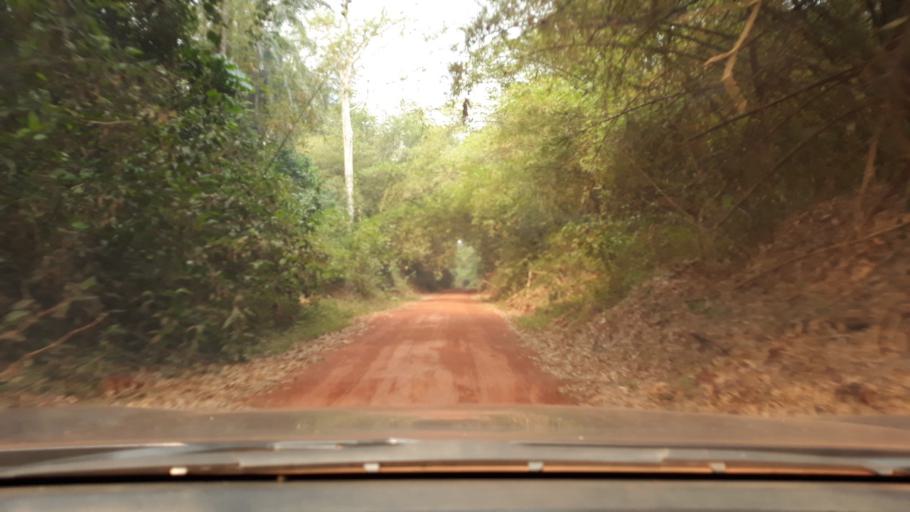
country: CD
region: Eastern Province
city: Aketi
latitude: 2.9176
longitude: 24.0643
